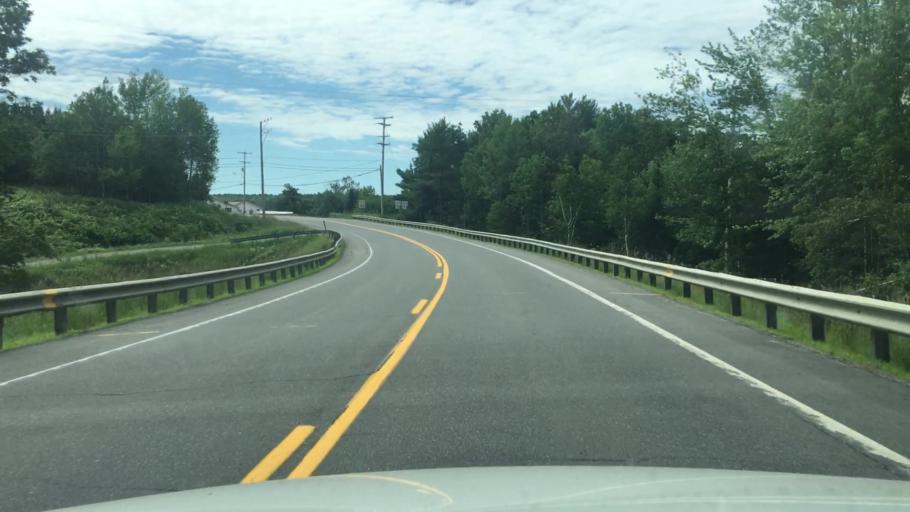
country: US
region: Maine
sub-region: Waldo County
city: Troy
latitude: 44.5818
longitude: -69.2793
